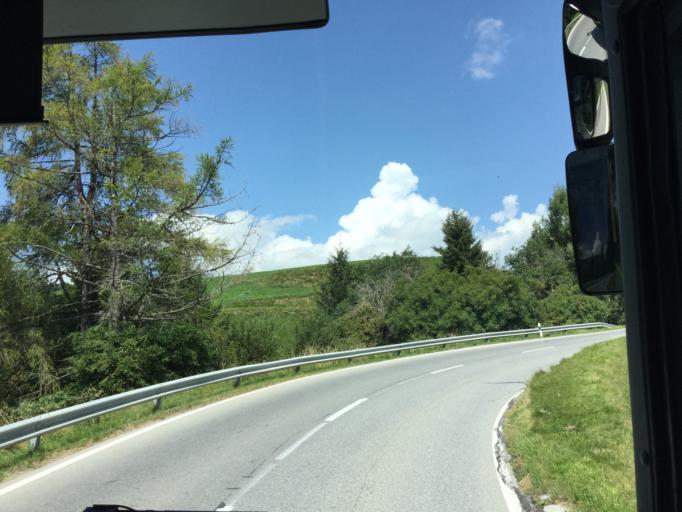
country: CH
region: Grisons
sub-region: Albula District
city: Tiefencastel
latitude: 46.6782
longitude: 9.5666
